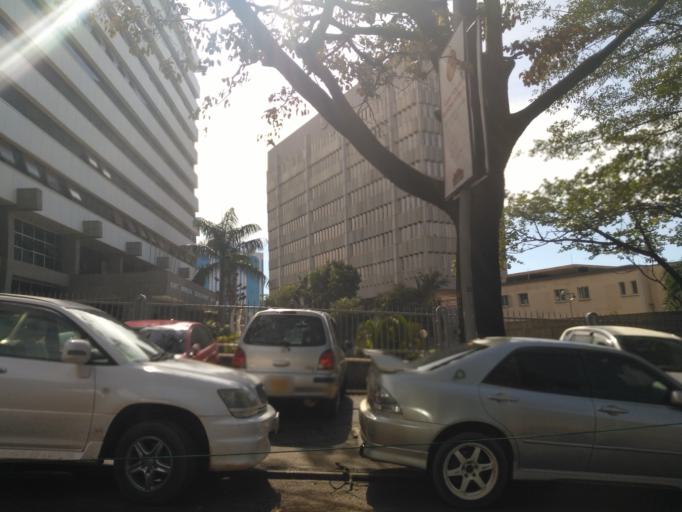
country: UG
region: Central Region
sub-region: Kampala District
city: Kampala
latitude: 0.3149
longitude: 32.5798
